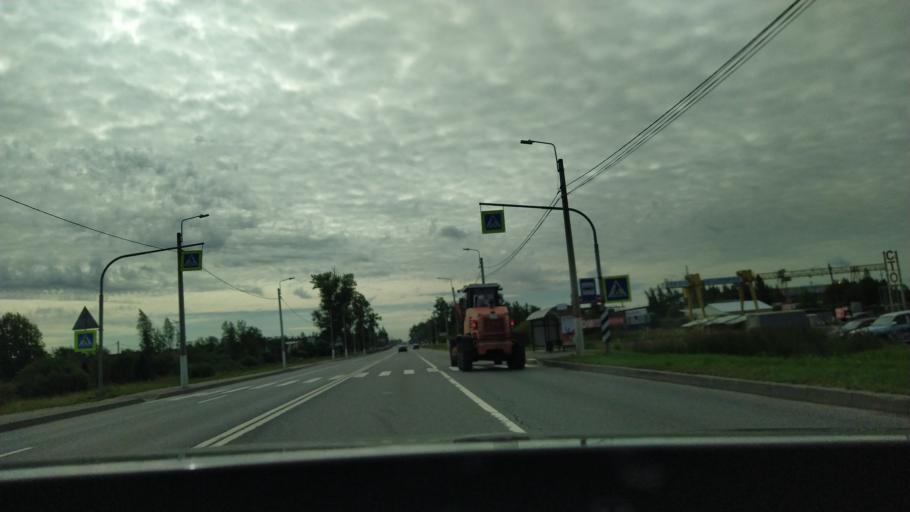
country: RU
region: Leningrad
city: Tosno
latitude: 59.5631
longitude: 30.8367
